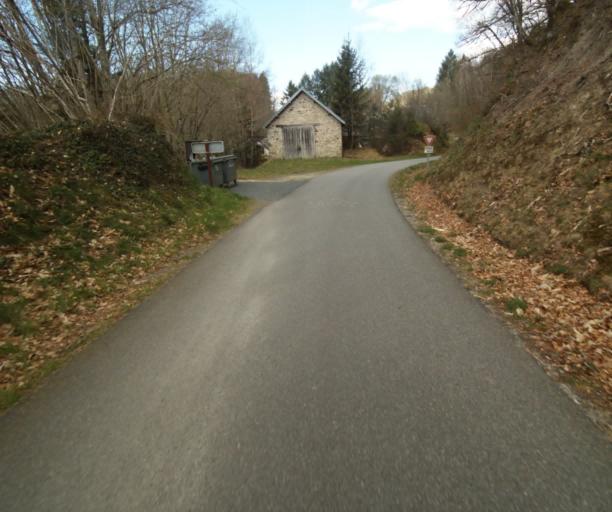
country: FR
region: Limousin
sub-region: Departement de la Correze
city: Laguenne
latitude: 45.2320
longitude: 1.8992
